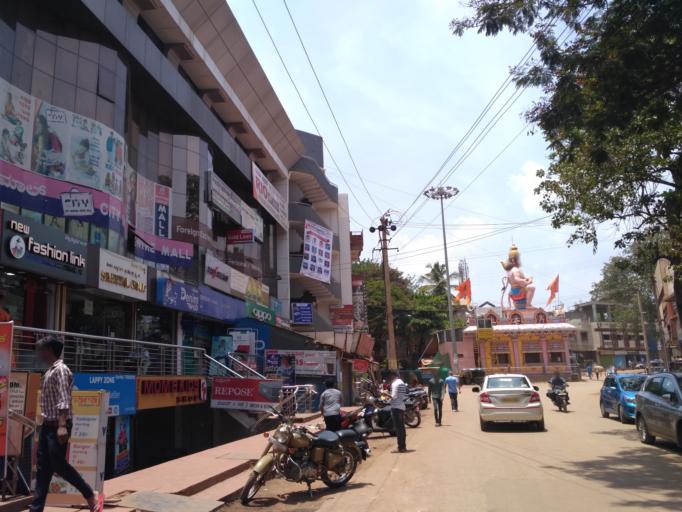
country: IN
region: Karnataka
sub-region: Dharwad
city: Hubli
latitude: 15.4549
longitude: 75.0101
